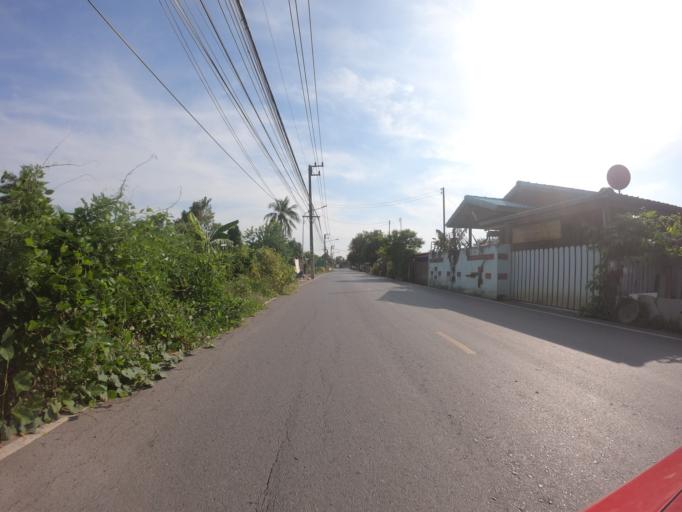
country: TH
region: Pathum Thani
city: Thanyaburi
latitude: 14.0044
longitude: 100.7310
